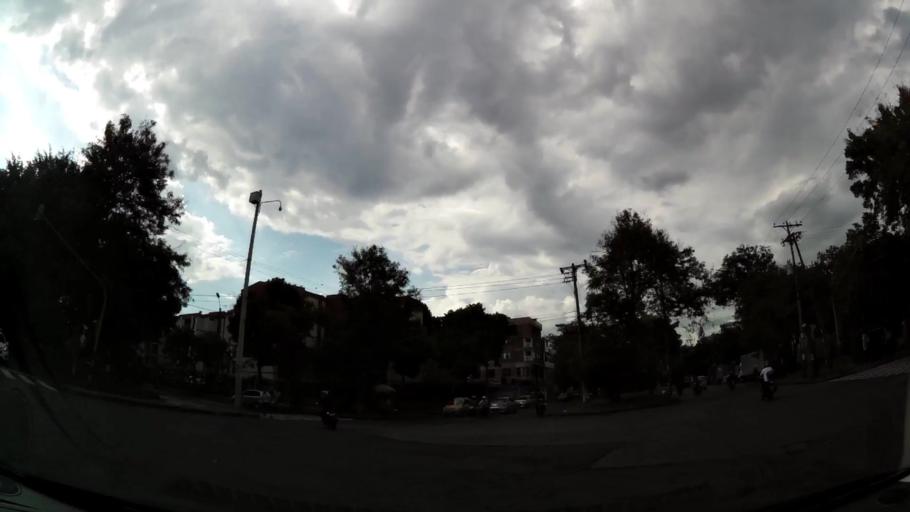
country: CO
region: Valle del Cauca
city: Cali
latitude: 3.4746
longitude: -76.4933
